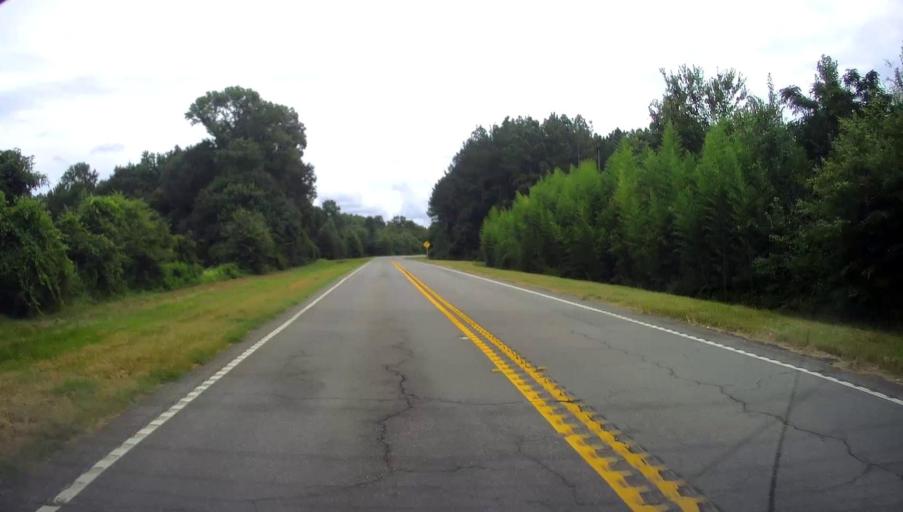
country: US
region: Georgia
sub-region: Macon County
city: Montezuma
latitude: 32.2943
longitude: -83.8971
